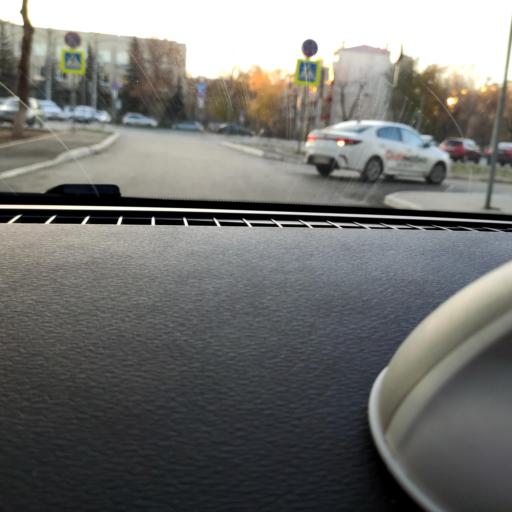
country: RU
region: Samara
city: Samara
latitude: 53.1999
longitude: 50.1621
